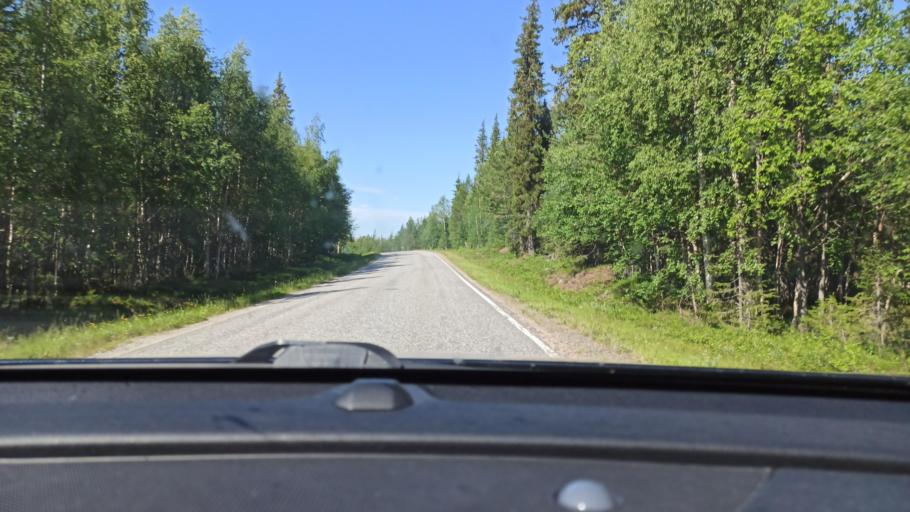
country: FI
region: Lapland
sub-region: Tunturi-Lappi
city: Kolari
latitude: 67.6836
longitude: 24.1253
